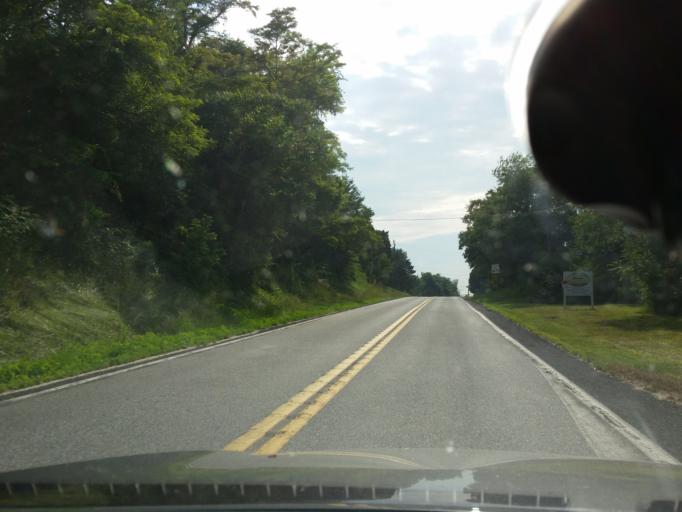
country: US
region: Pennsylvania
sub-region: Perry County
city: Duncannon
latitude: 40.3258
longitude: -77.0495
